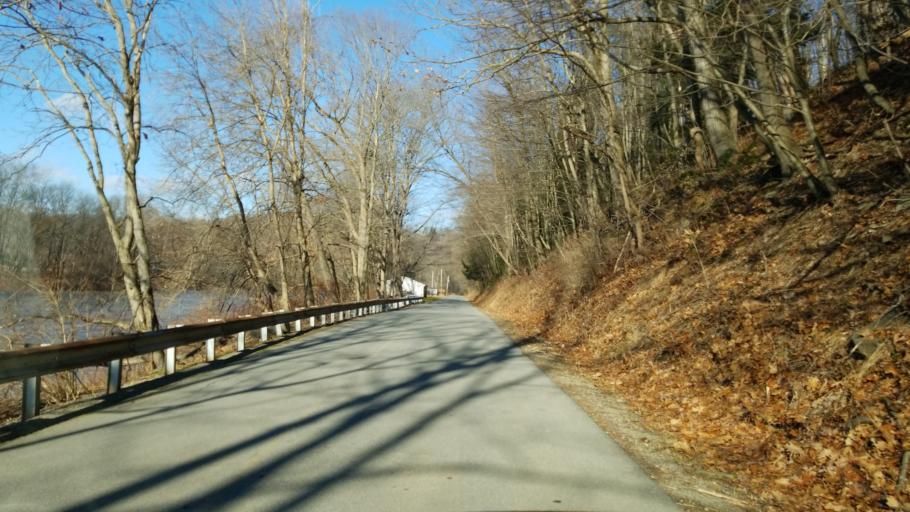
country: US
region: Pennsylvania
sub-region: Clearfield County
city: Curwensville
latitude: 40.9756
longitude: -78.4910
